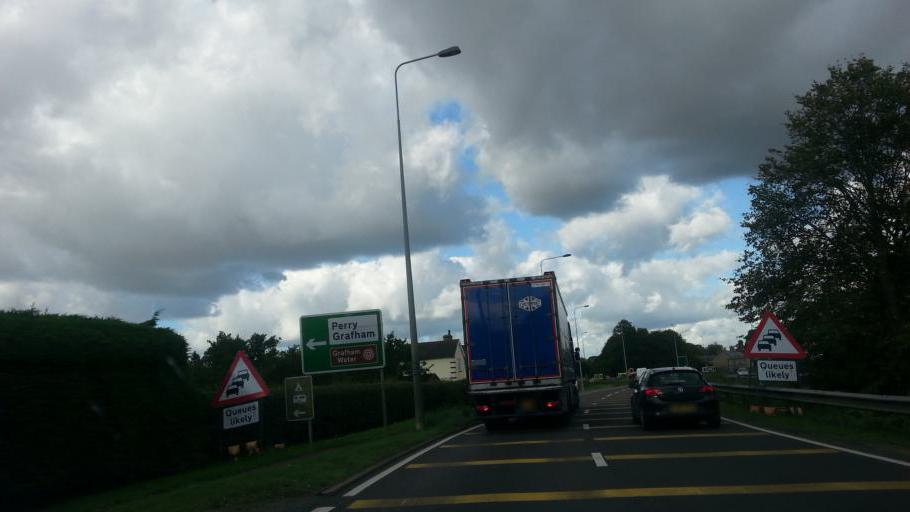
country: GB
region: England
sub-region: Cambridgeshire
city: Buckden
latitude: 52.2900
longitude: -0.2572
